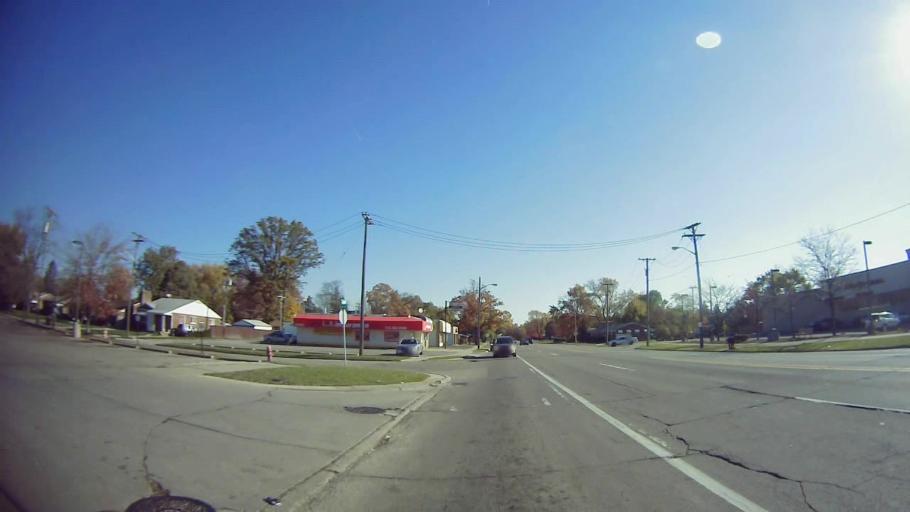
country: US
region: Michigan
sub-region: Wayne County
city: Dearborn Heights
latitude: 42.3570
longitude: -83.2742
